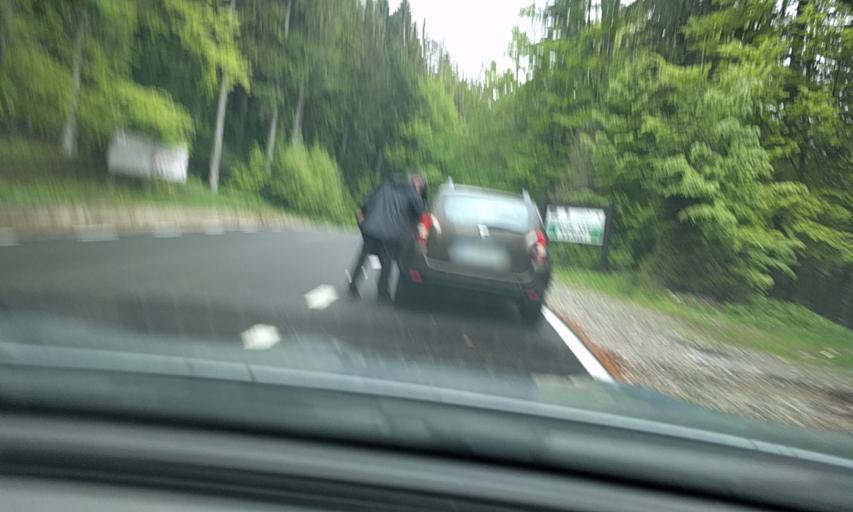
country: RO
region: Prahova
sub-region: Oras Sinaia
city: Sinaia
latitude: 45.3112
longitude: 25.5208
